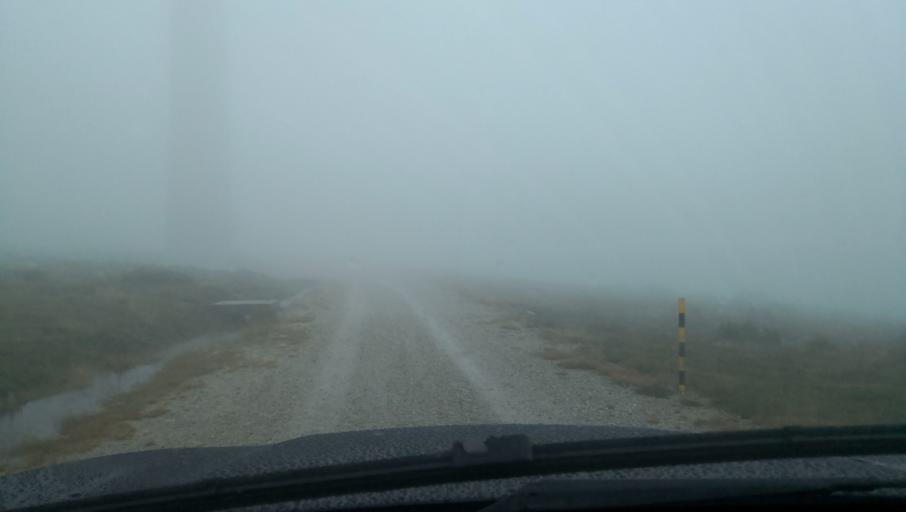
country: PT
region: Vila Real
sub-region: Vila Real
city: Vila Real
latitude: 41.3439
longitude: -7.8420
